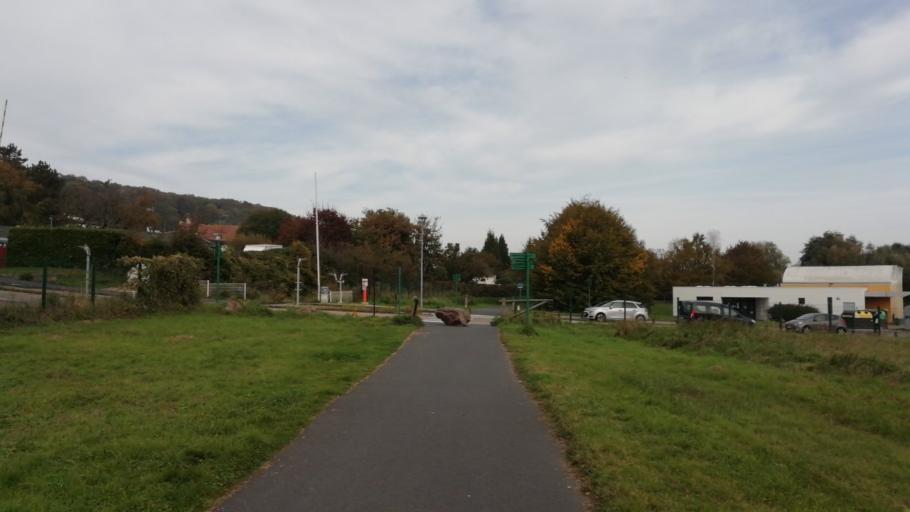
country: FR
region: Haute-Normandie
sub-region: Departement de la Seine-Maritime
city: Harfleur
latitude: 49.5112
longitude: 0.1902
